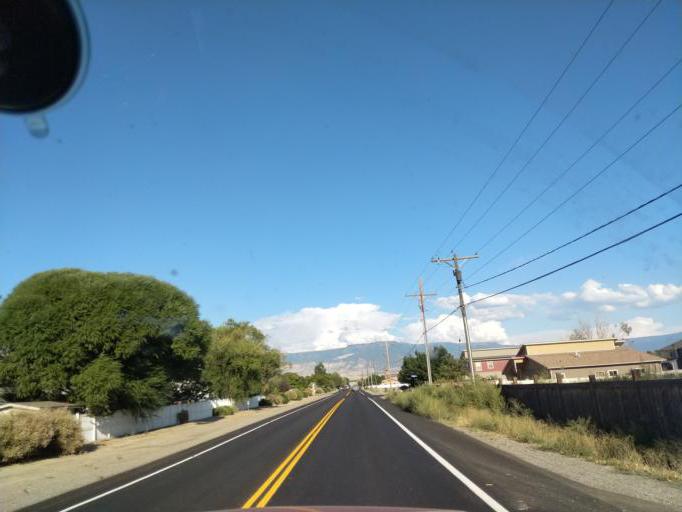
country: US
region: Colorado
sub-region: Mesa County
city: Fruitvale
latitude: 39.0629
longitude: -108.4710
